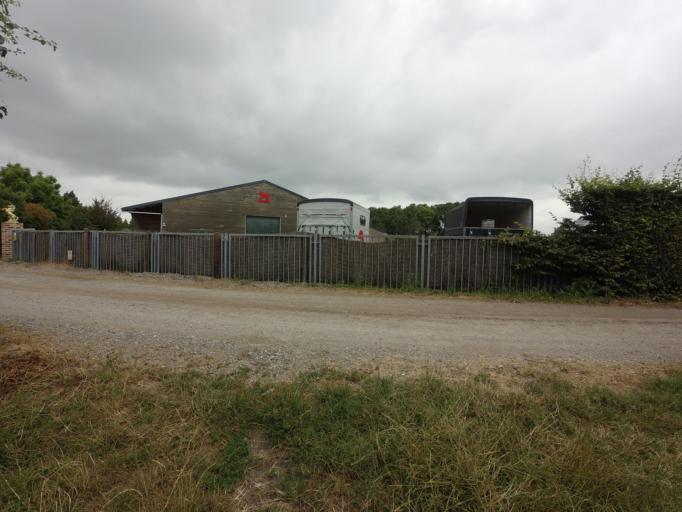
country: NL
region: Limburg
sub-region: Valkenburg aan de Geul
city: Berg
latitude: 50.8232
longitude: 5.7768
